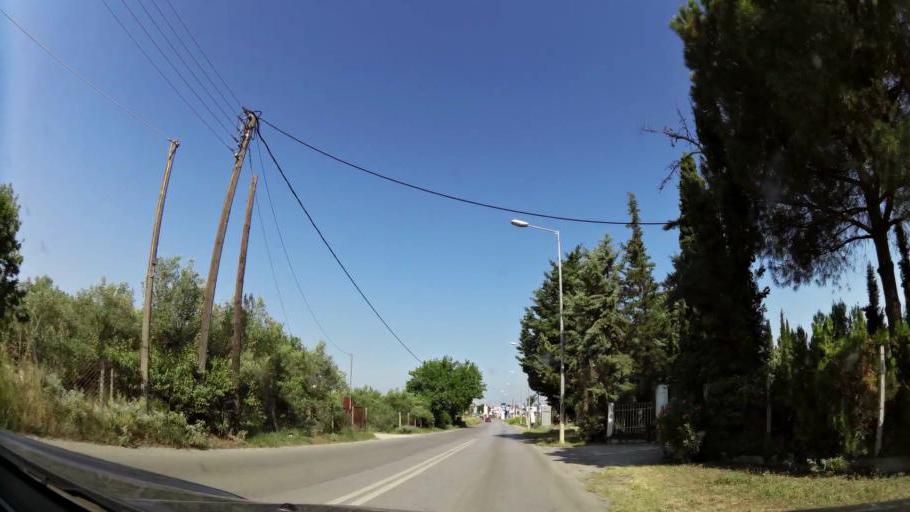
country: GR
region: Central Macedonia
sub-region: Nomos Thessalonikis
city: Neo Rysi
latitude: 40.4964
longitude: 22.9956
